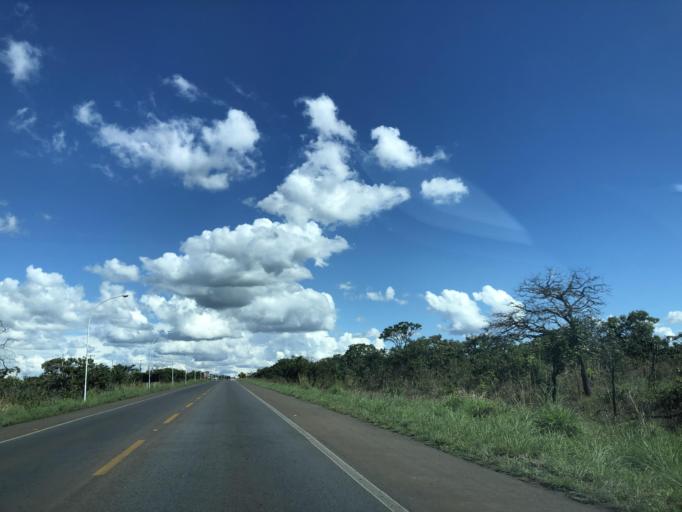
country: BR
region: Federal District
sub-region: Brasilia
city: Brasilia
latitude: -15.6655
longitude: -47.8869
